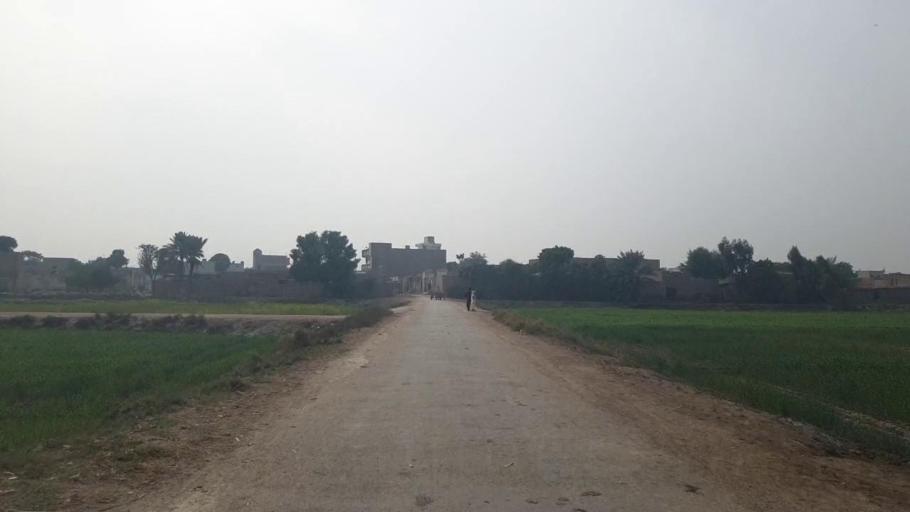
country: PK
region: Sindh
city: Tando Adam
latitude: 25.7795
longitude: 68.6687
